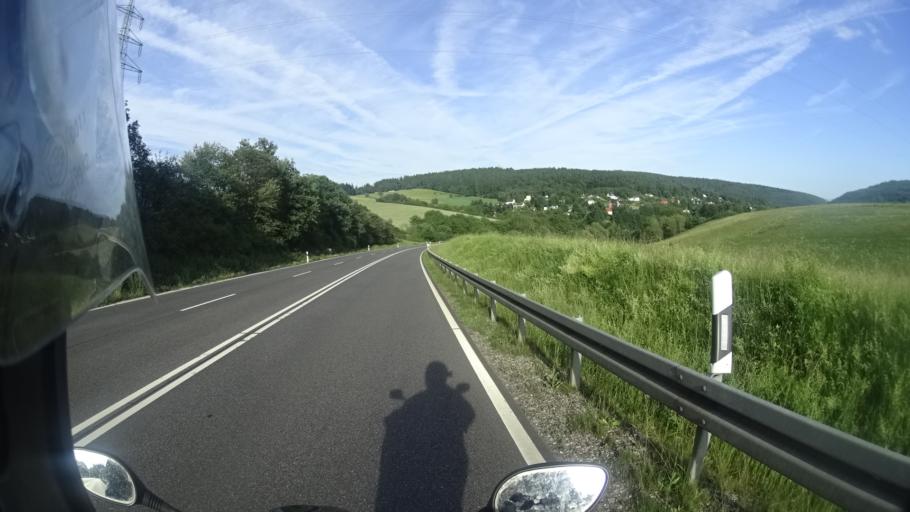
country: DE
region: Hesse
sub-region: Regierungsbezirk Darmstadt
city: Schlangenbad
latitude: 50.1179
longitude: 8.0910
